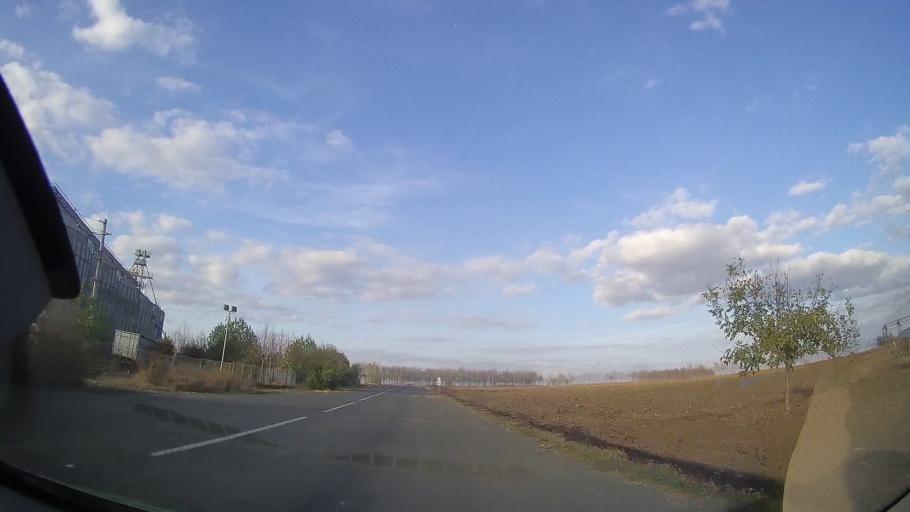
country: RO
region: Constanta
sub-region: Comuna Dumbraveni
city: Dumbraveni
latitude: 43.9264
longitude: 28.0297
